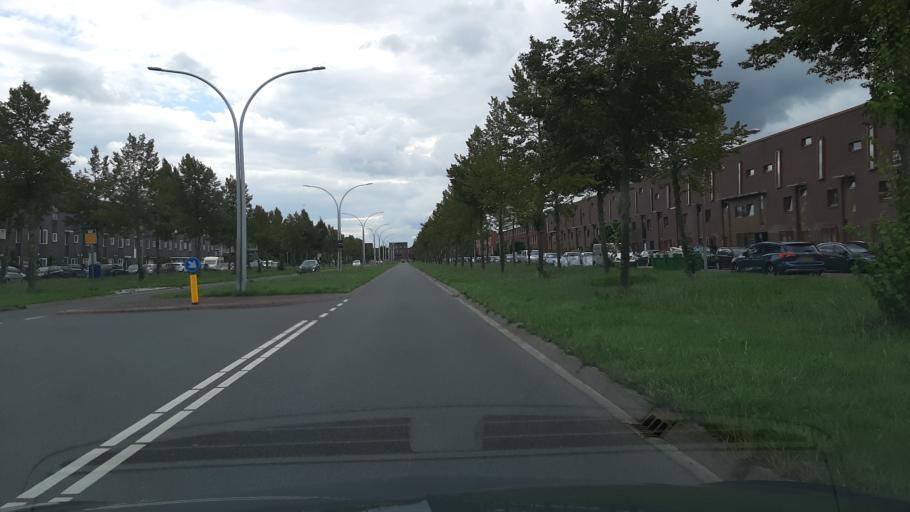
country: NL
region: Overijssel
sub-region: Gemeente Zwolle
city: Zwolle
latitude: 52.5419
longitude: 6.0523
